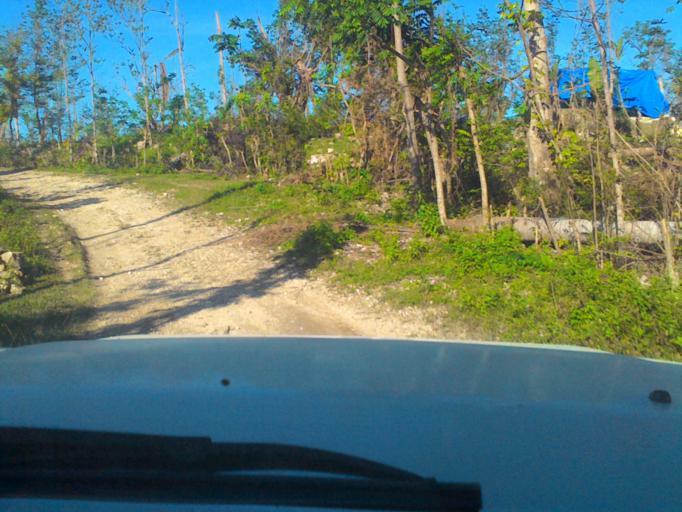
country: HT
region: Grandans
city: Jeremie
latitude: 18.5149
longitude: -74.0818
